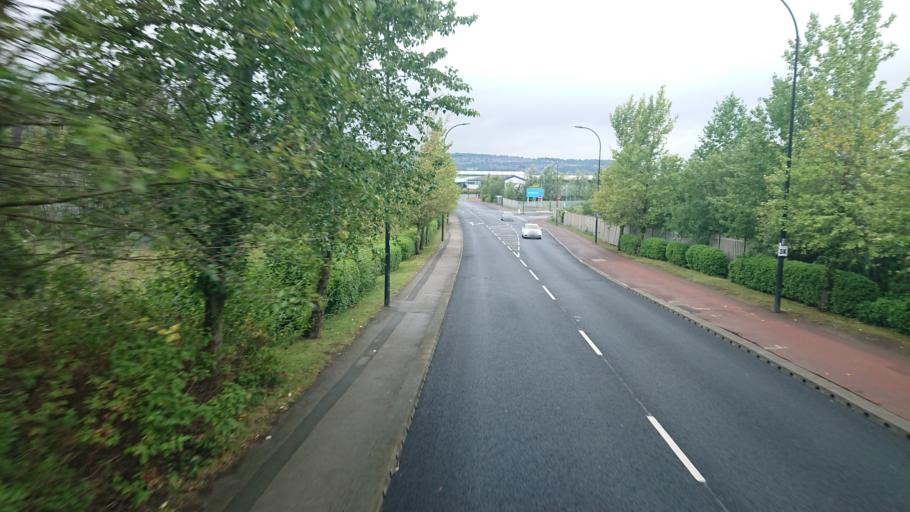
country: GB
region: England
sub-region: Rotherham
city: Orgreave
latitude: 53.3978
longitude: -1.4019
